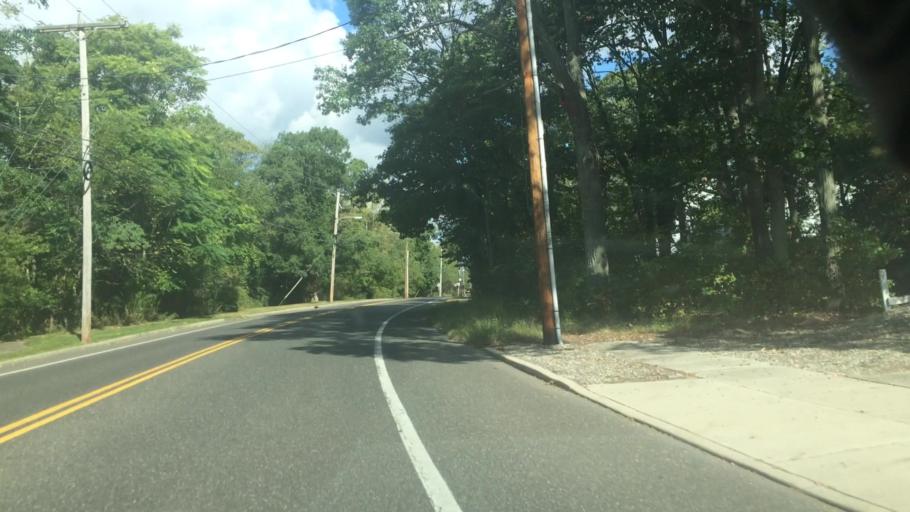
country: US
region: New Jersey
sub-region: Ocean County
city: Toms River
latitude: 39.9845
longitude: -74.1724
